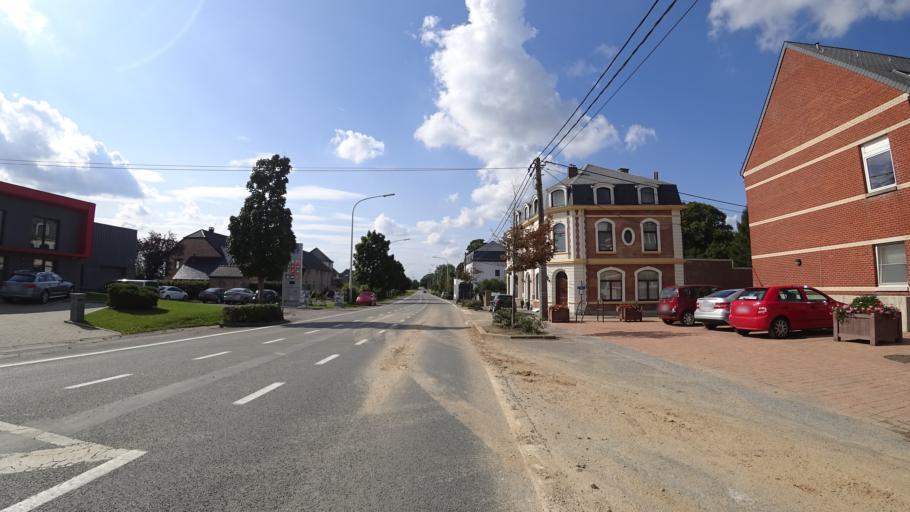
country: BE
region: Wallonia
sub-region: Province de Namur
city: Floreffe
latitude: 50.4874
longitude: 4.7546
